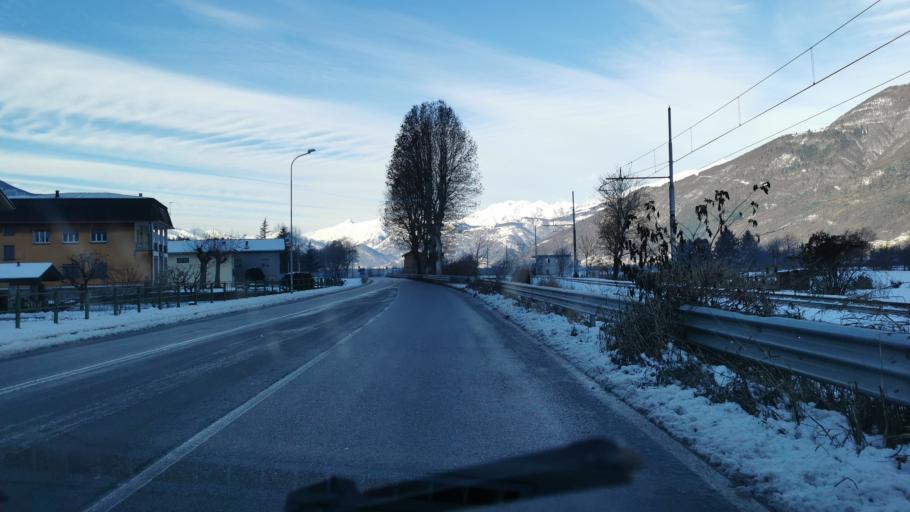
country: IT
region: Lombardy
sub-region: Provincia di Sondrio
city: Rogolo
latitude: 46.1379
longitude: 9.5009
